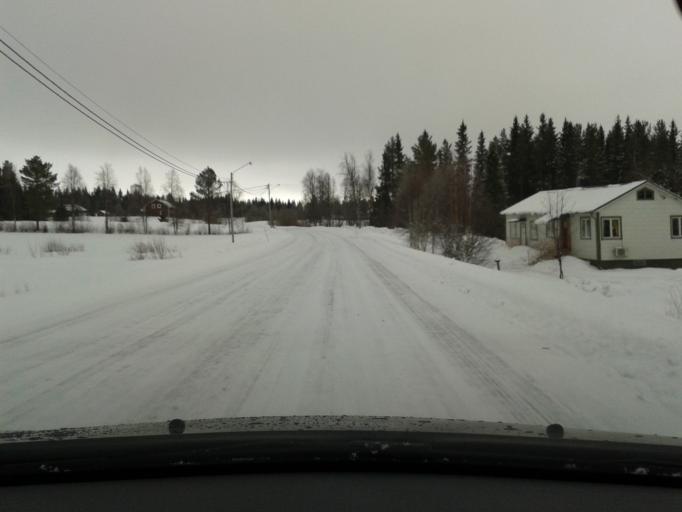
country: SE
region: Vaesterbotten
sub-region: Vilhelmina Kommun
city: Sjoberg
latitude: 64.8338
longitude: 15.9318
